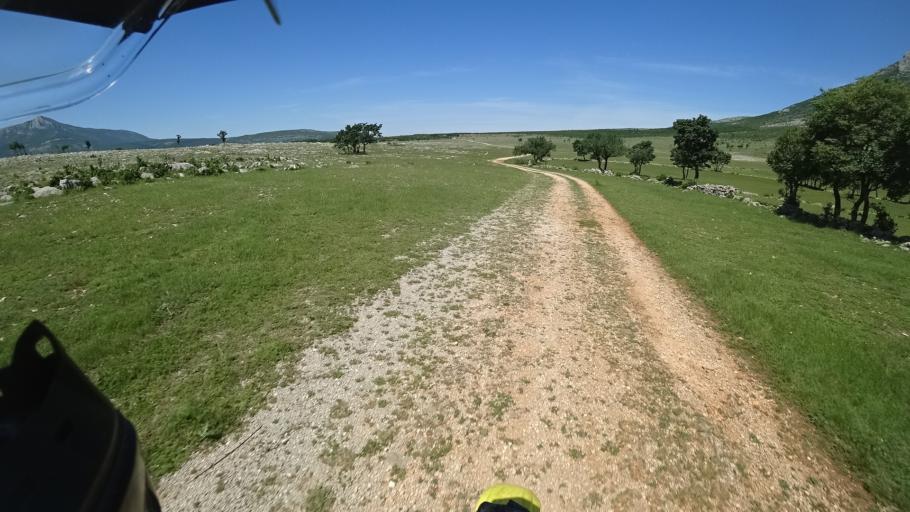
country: BA
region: Federation of Bosnia and Herzegovina
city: Bosansko Grahovo
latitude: 44.0031
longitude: 16.4001
